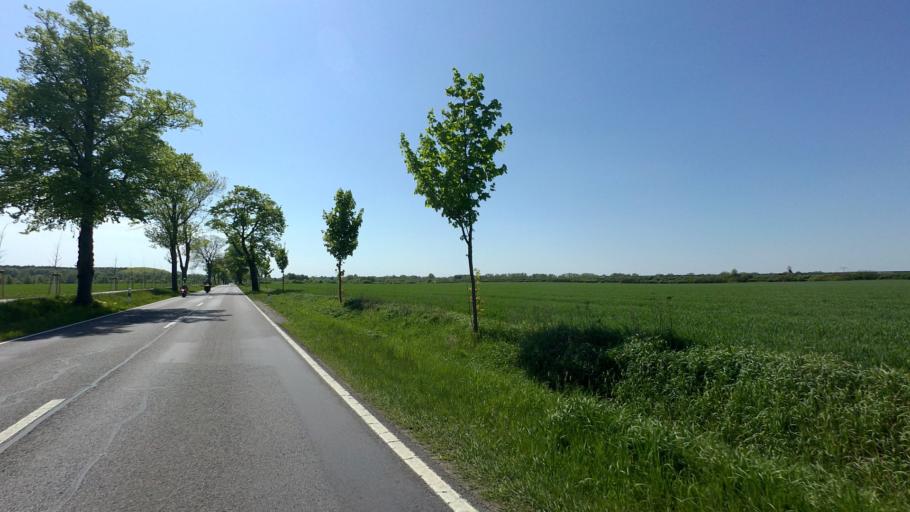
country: DE
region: Brandenburg
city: Schulzendorf
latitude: 52.3562
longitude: 13.5574
